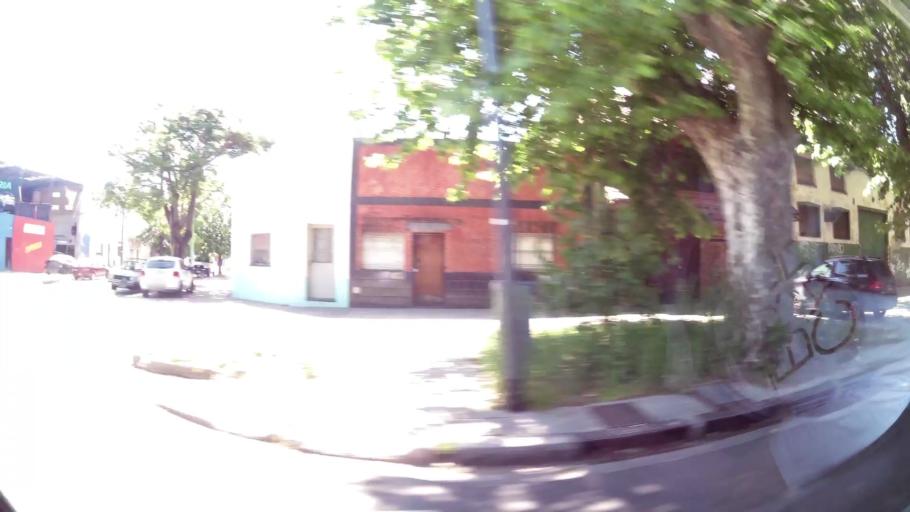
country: AR
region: Buenos Aires F.D.
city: Villa Lugano
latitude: -34.6629
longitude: -58.4361
